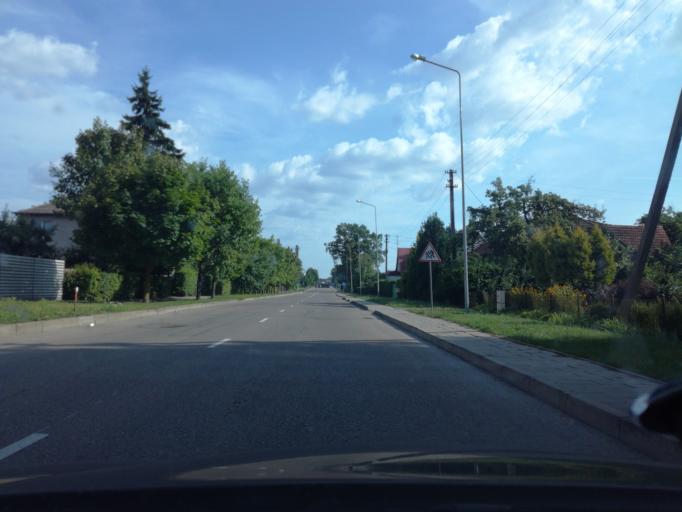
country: LT
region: Marijampoles apskritis
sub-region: Marijampole Municipality
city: Marijampole
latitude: 54.5433
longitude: 23.3488
